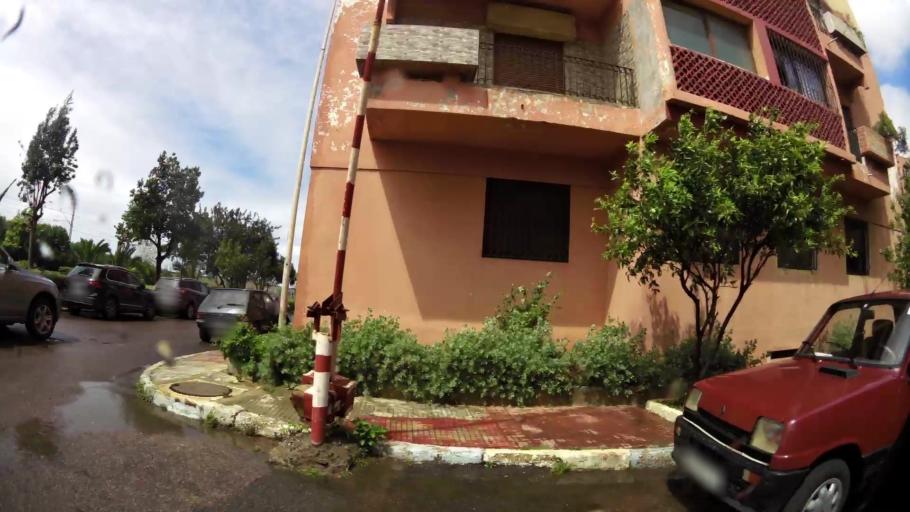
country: MA
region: Grand Casablanca
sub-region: Casablanca
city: Casablanca
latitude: 33.5325
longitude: -7.6534
